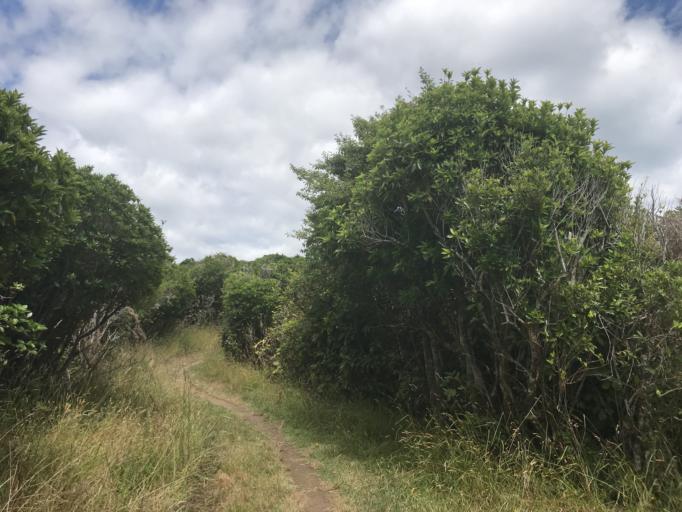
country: NZ
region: Marlborough
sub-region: Marlborough District
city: Picton
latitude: -41.2111
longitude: 174.0138
